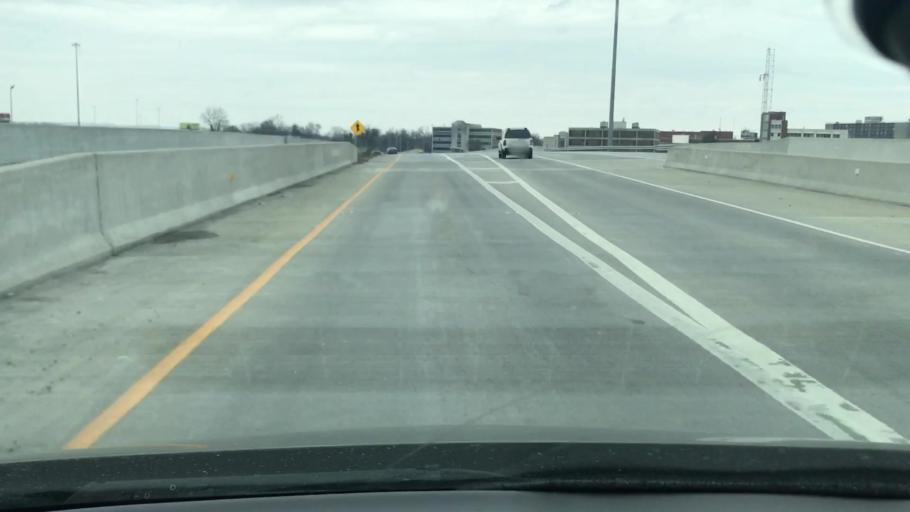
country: US
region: Indiana
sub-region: Clark County
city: Jeffersonville
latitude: 38.2780
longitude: -85.7491
